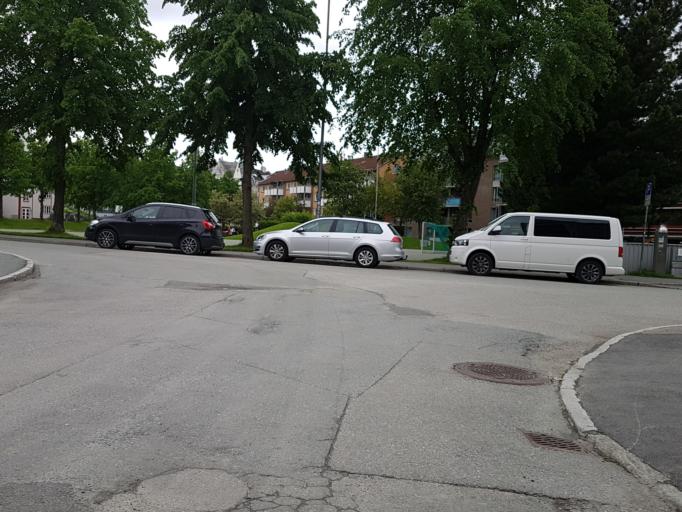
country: NO
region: Sor-Trondelag
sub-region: Trondheim
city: Trondheim
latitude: 63.4356
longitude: 10.4240
